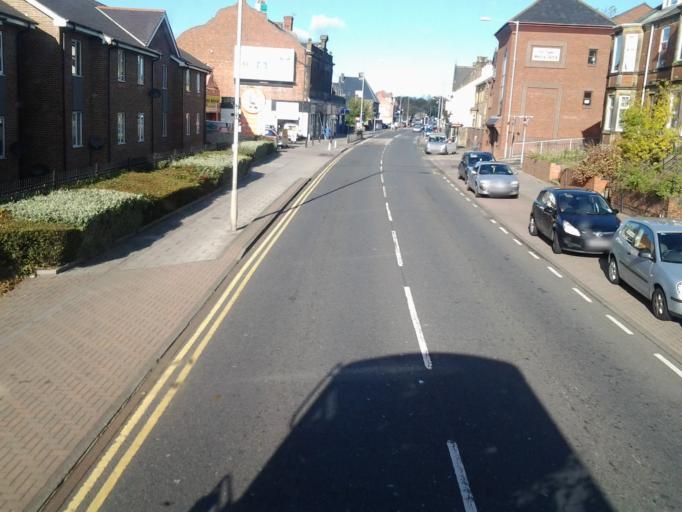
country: GB
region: England
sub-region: Gateshead
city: Lamesley
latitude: 54.9333
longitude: -1.5988
